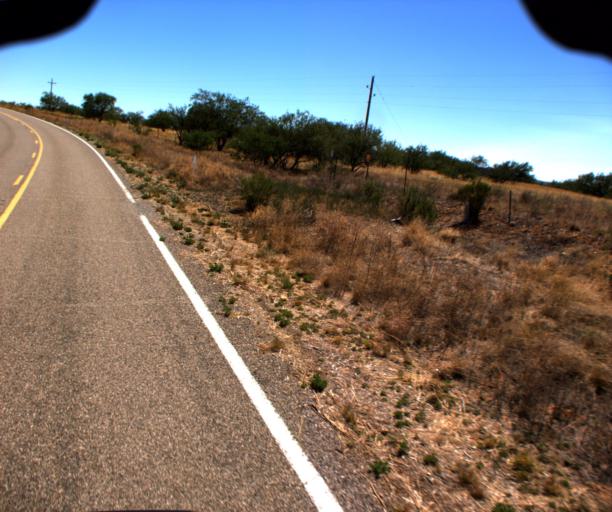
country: US
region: Arizona
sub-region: Pima County
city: Sells
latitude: 31.5792
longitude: -111.5371
